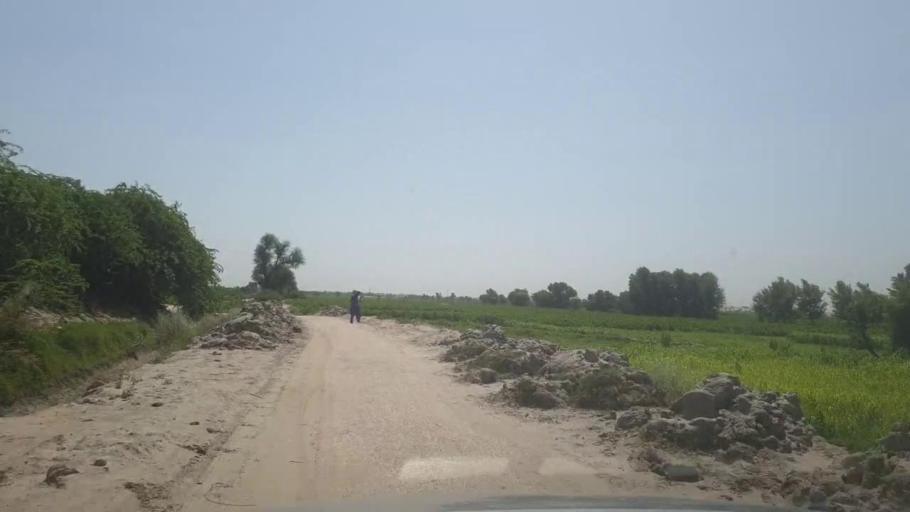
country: PK
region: Sindh
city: Khairpur
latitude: 27.3516
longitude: 69.0467
